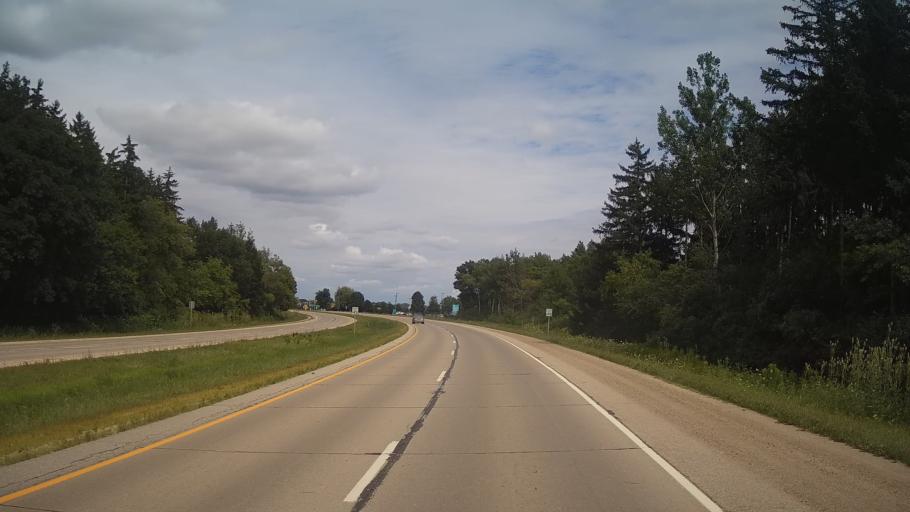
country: US
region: Wisconsin
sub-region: Winnebago County
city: Oshkosh
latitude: 44.0282
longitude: -88.6005
